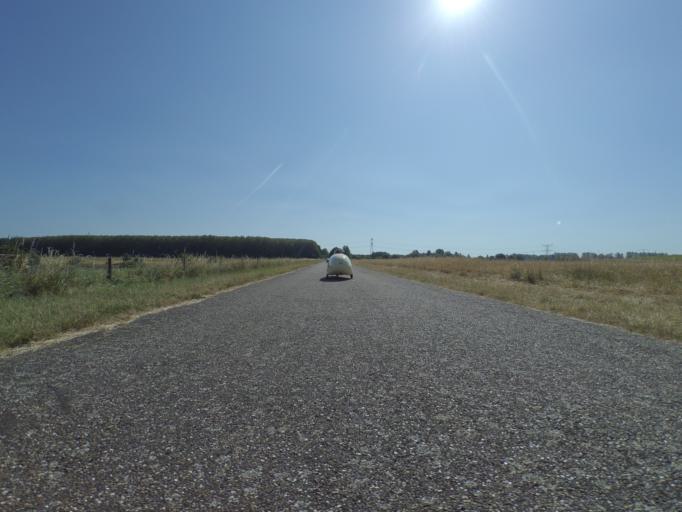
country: NL
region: North Brabant
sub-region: Gemeente Woensdrecht
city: Woensdrecht
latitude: 51.3971
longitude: 4.2285
